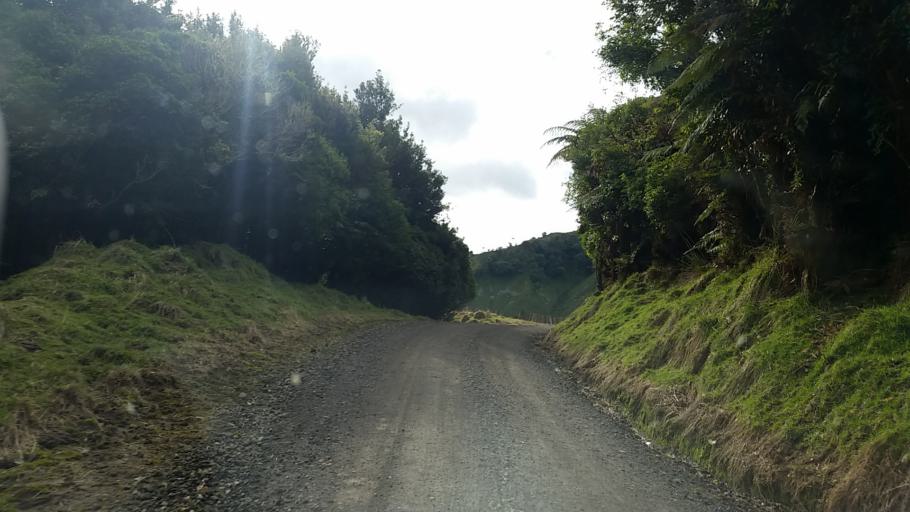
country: NZ
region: Taranaki
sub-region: South Taranaki District
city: Eltham
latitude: -39.1715
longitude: 174.6113
